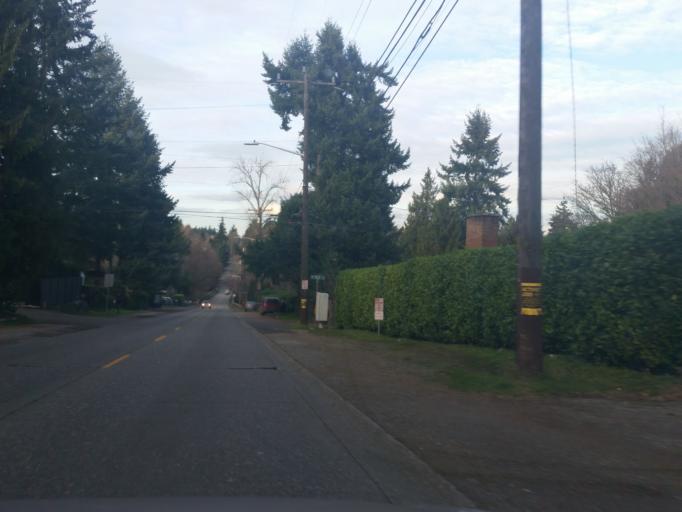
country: US
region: Washington
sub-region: King County
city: Shoreline
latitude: 47.7027
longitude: -122.3124
